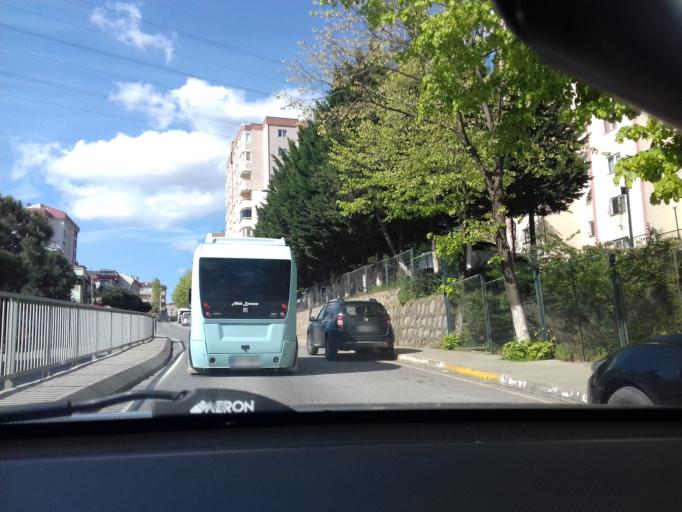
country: TR
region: Istanbul
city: Pendik
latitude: 40.9111
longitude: 29.2825
